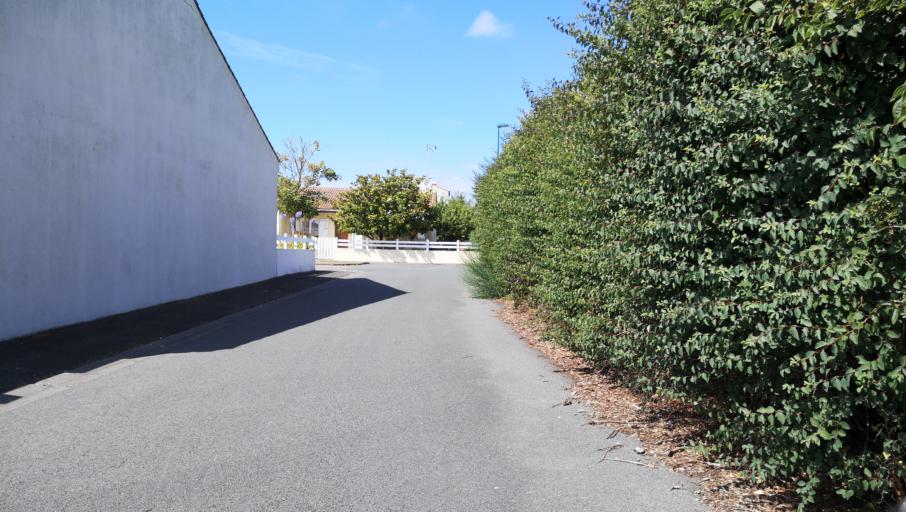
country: FR
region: Pays de la Loire
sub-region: Departement de la Vendee
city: Les Sables-d'Olonne
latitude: 46.5183
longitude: -1.7915
